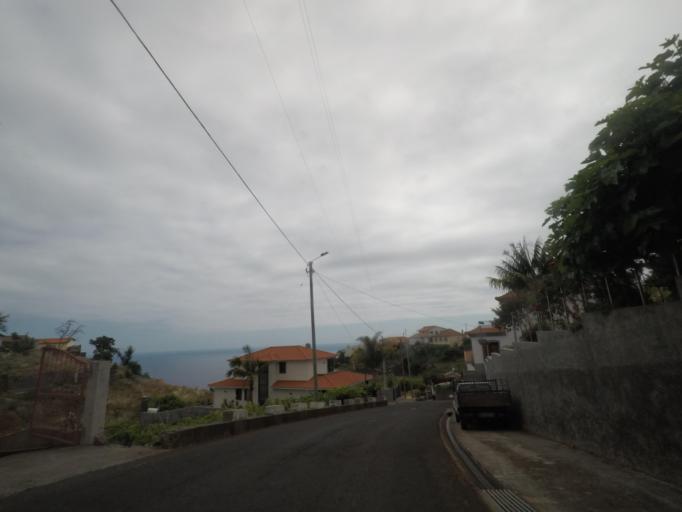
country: PT
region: Madeira
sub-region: Calheta
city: Estreito da Calheta
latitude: 32.7347
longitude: -17.1730
